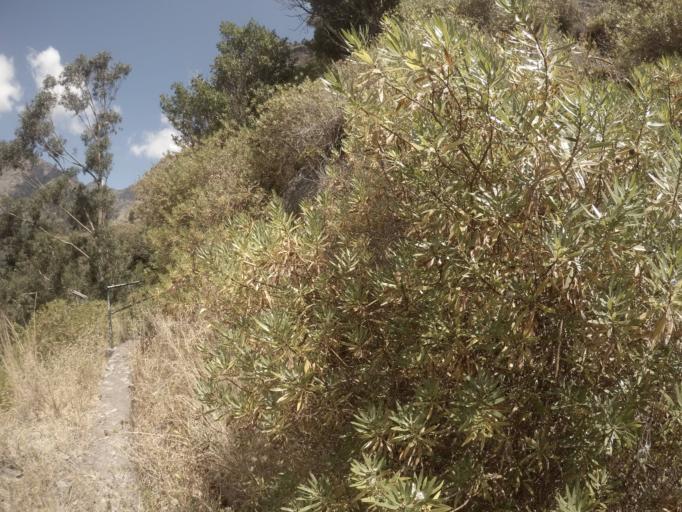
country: PT
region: Madeira
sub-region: Camara de Lobos
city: Curral das Freiras
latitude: 32.7023
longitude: -16.9641
